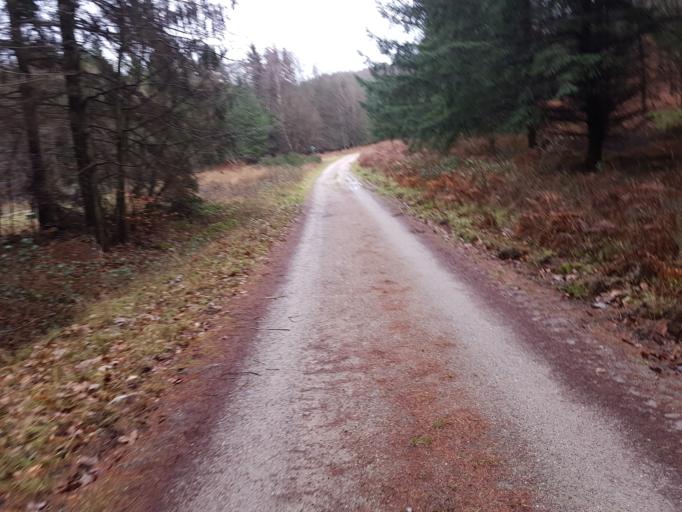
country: DE
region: Mecklenburg-Vorpommern
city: Ostseebad Binz
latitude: 54.3906
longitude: 13.6273
